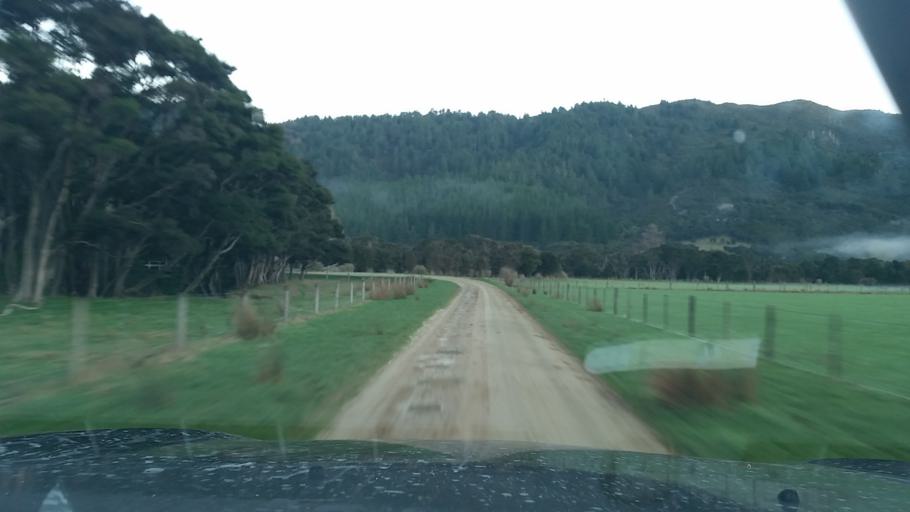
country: NZ
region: Marlborough
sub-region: Marlborough District
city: Picton
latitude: -41.1580
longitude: 174.1329
